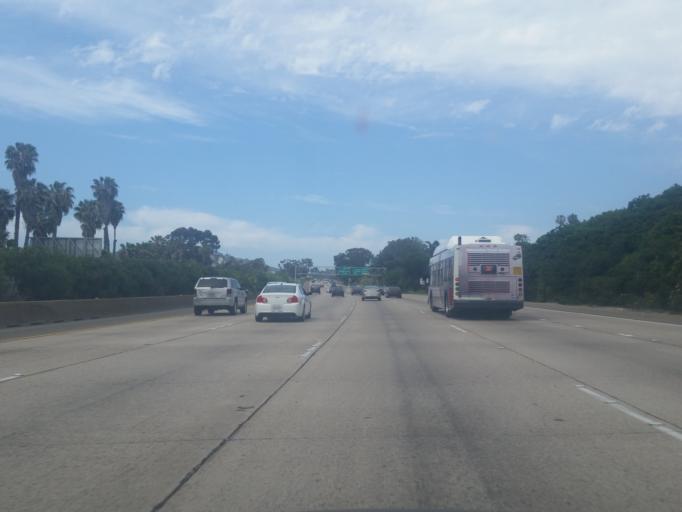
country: US
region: California
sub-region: San Diego County
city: La Jolla
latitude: 32.7945
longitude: -117.2080
